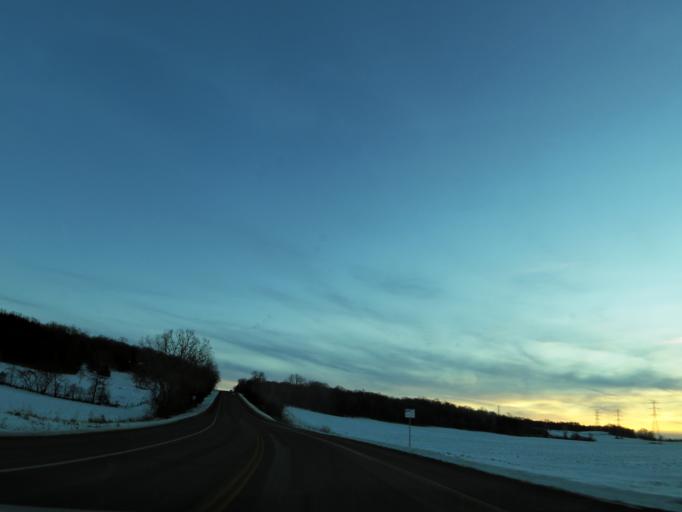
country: US
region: Minnesota
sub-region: Scott County
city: Shakopee
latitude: 44.7727
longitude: -93.5610
